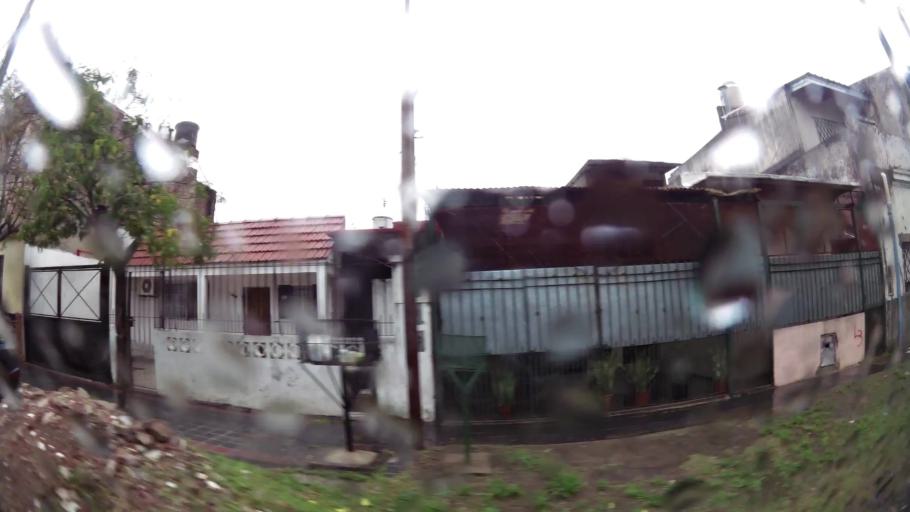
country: AR
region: Buenos Aires
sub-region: Partido de Lanus
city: Lanus
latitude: -34.7193
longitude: -58.4067
